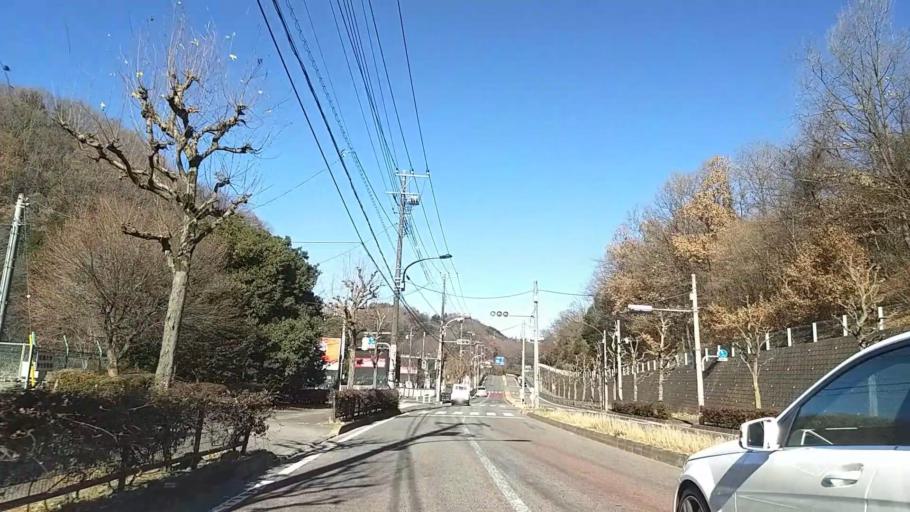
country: JP
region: Tokyo
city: Hachioji
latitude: 35.6256
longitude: 139.2852
